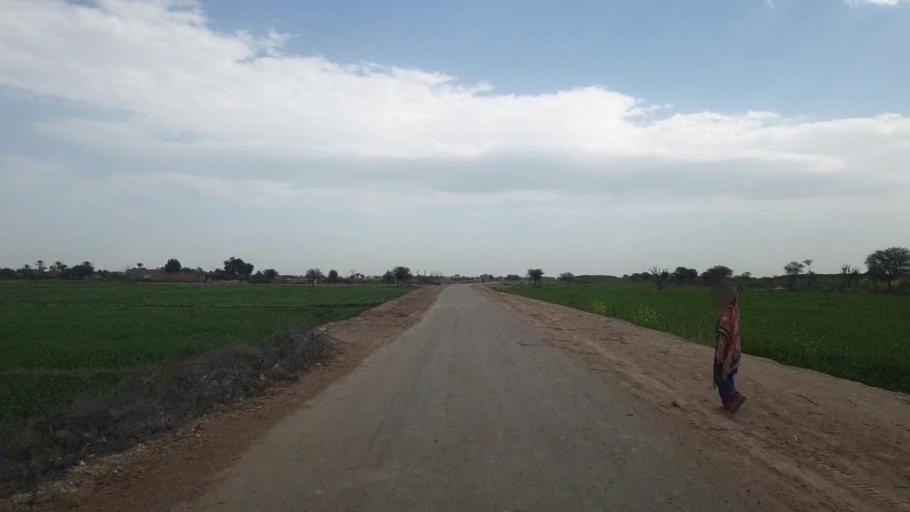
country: PK
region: Sindh
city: Hala
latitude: 25.9800
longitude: 68.4143
